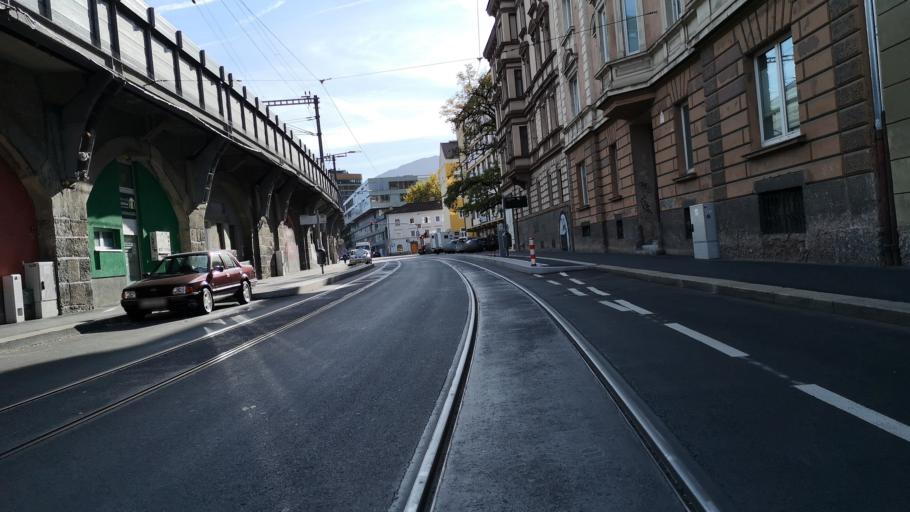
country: AT
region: Tyrol
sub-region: Innsbruck Stadt
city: Innsbruck
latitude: 47.2698
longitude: 11.4030
